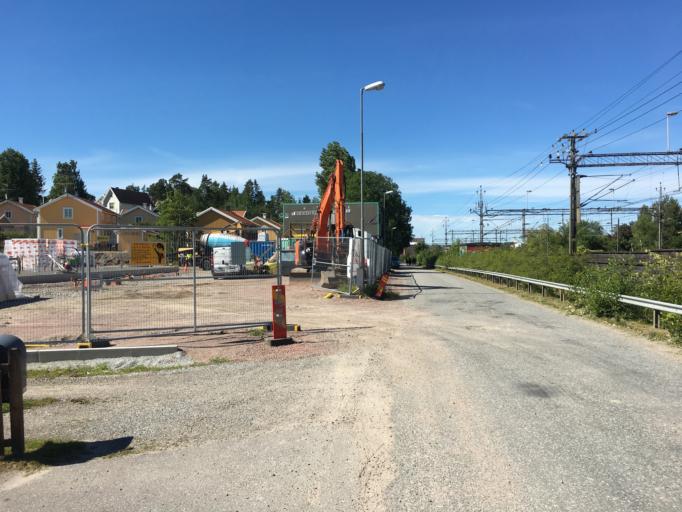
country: SE
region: Stockholm
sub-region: Sollentuna Kommun
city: Sollentuna
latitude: 59.4172
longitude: 17.9564
